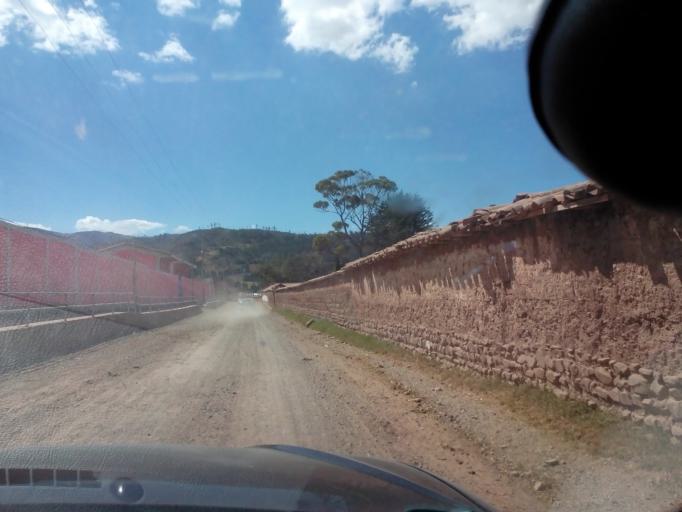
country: PE
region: Cusco
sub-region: Provincia de Anta
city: Huarocondo
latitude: -13.4185
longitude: -72.2096
